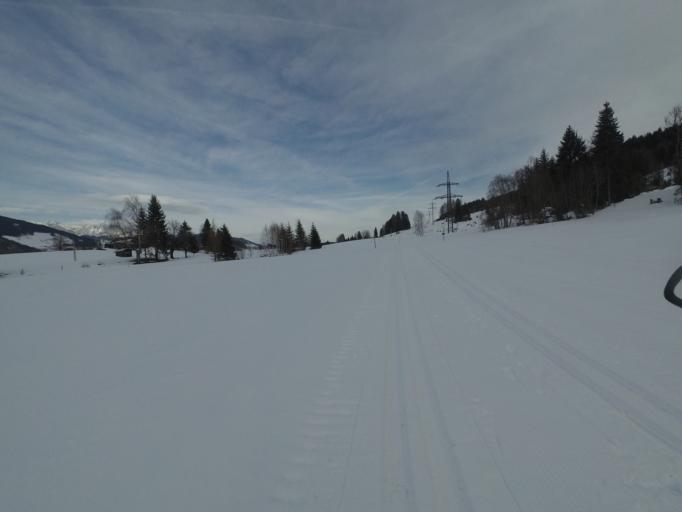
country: AT
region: Salzburg
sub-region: Politischer Bezirk Zell am See
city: Taxenbach
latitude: 47.2845
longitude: 12.9885
